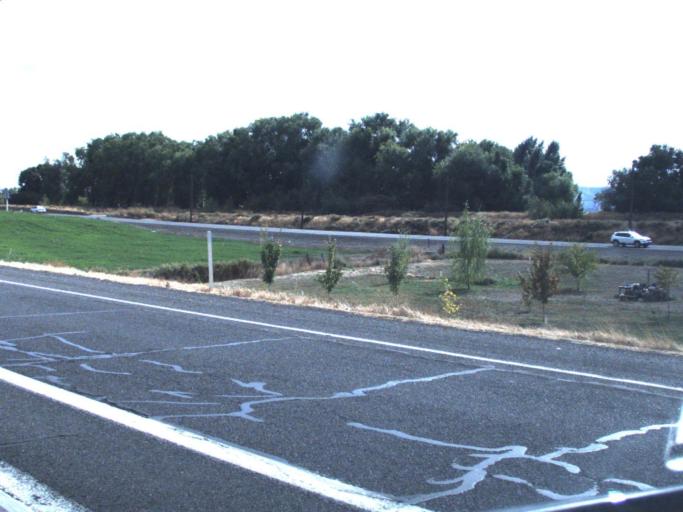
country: US
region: Washington
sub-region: Yakima County
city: Zillah
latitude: 46.3888
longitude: -120.2362
